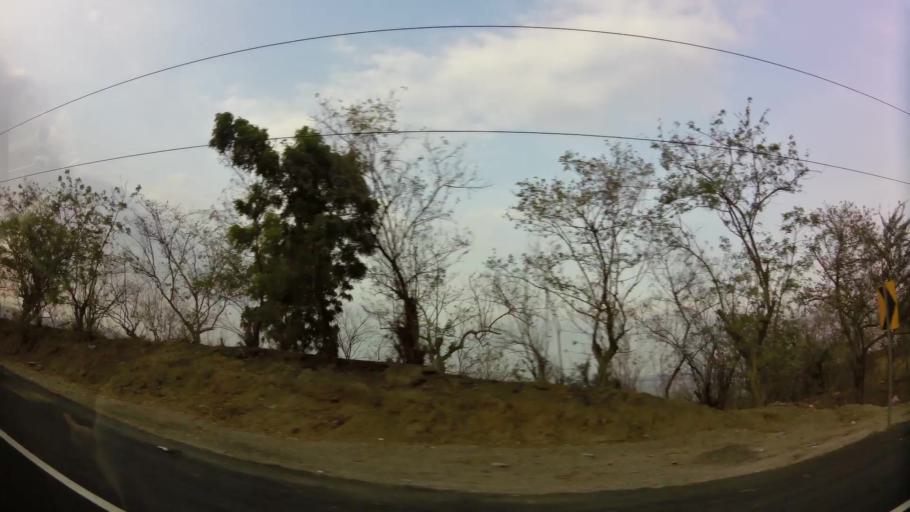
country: NI
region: Leon
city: Nagarote
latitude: 12.2496
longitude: -86.4462
